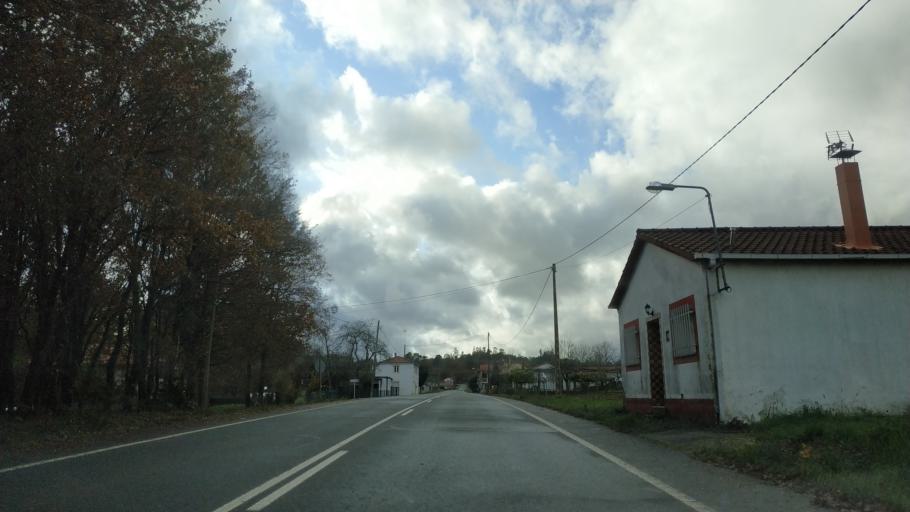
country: ES
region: Galicia
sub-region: Provincia da Coruna
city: Arzua
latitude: 42.8833
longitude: -8.1878
